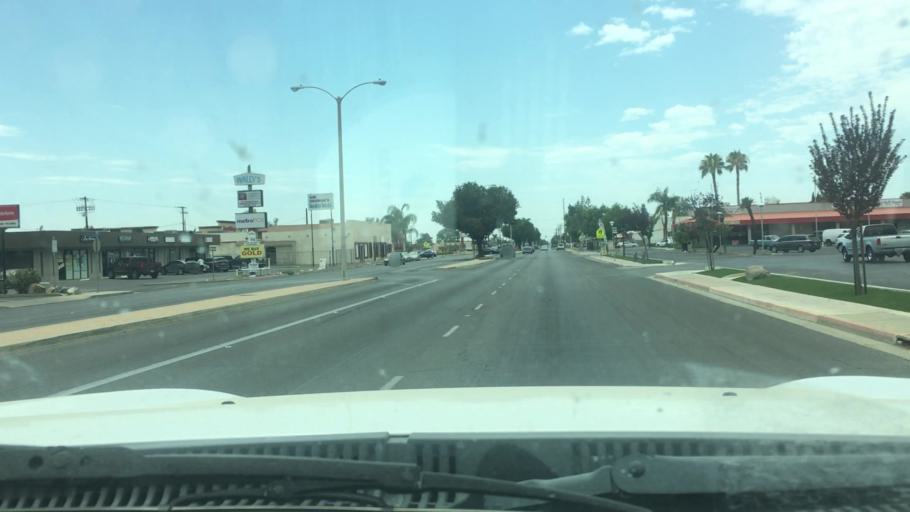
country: US
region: California
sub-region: Tulare County
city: Porterville
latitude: 36.0659
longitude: -119.0467
